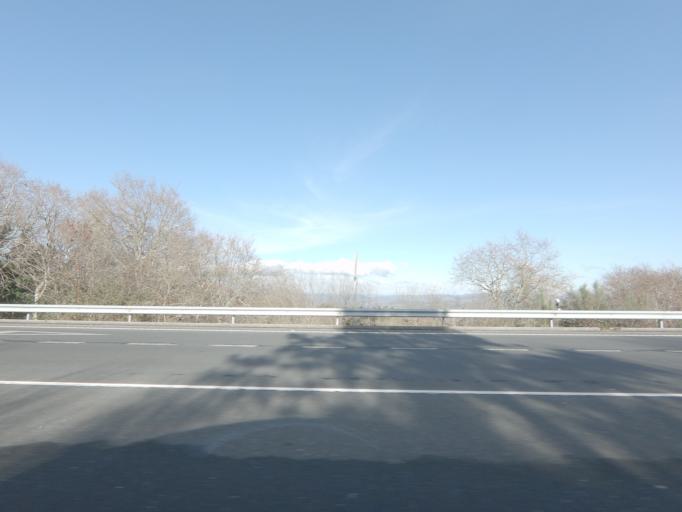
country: ES
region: Galicia
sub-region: Provincia de Pontevedra
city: Silleda
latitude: 42.7064
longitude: -8.3455
